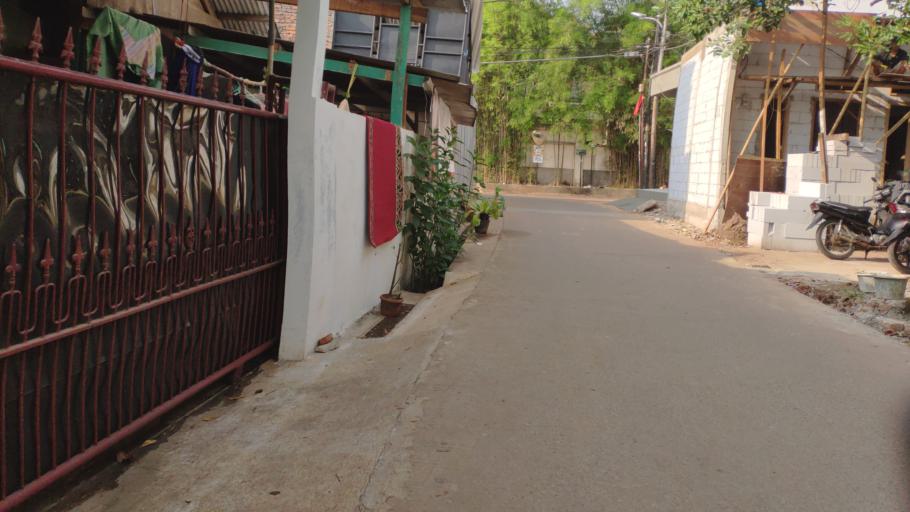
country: ID
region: West Java
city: Pamulang
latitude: -6.3081
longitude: 106.8058
